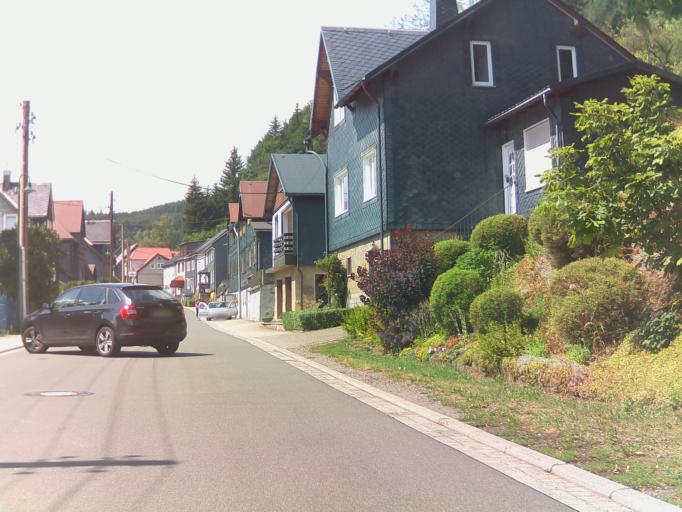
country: DE
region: Thuringia
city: Altenfeld
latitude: 50.5652
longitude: 10.9687
